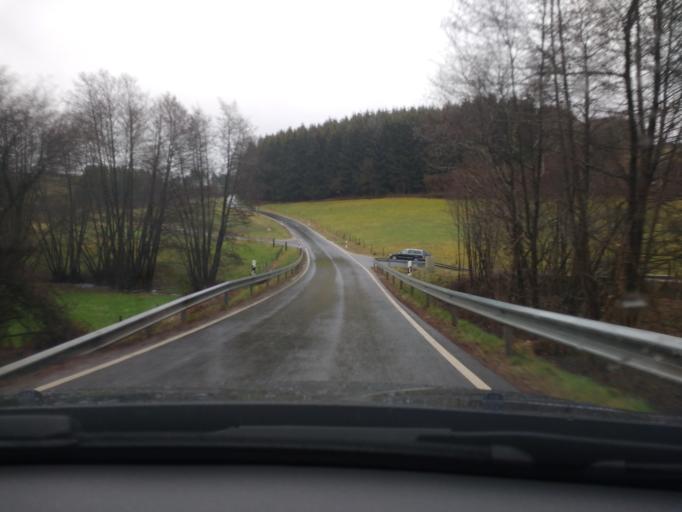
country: DE
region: Rheinland-Pfalz
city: Paschel
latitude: 49.6335
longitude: 6.6818
